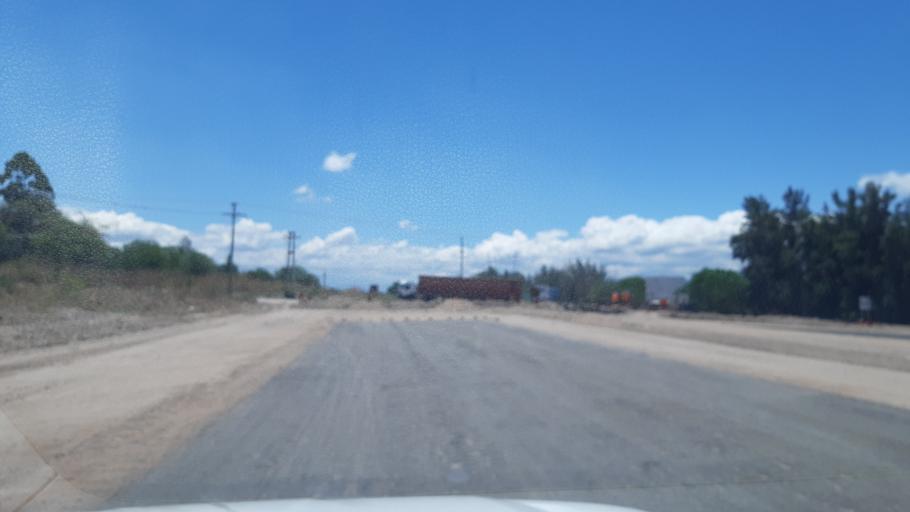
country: AR
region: Jujuy
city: La Mendieta
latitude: -24.4728
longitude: -65.0390
